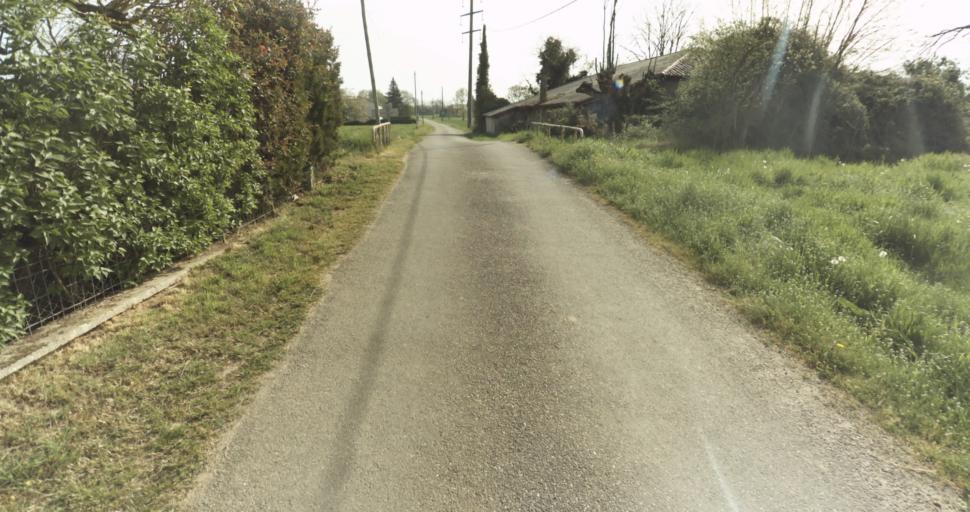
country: FR
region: Midi-Pyrenees
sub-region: Departement du Tarn-et-Garonne
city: Moissac
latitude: 44.1146
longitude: 1.1221
